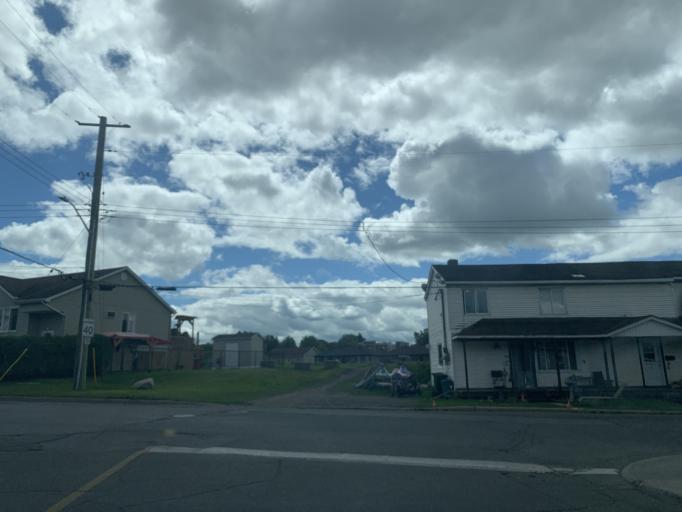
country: CA
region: Ontario
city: Hawkesbury
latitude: 45.6076
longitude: -74.6092
